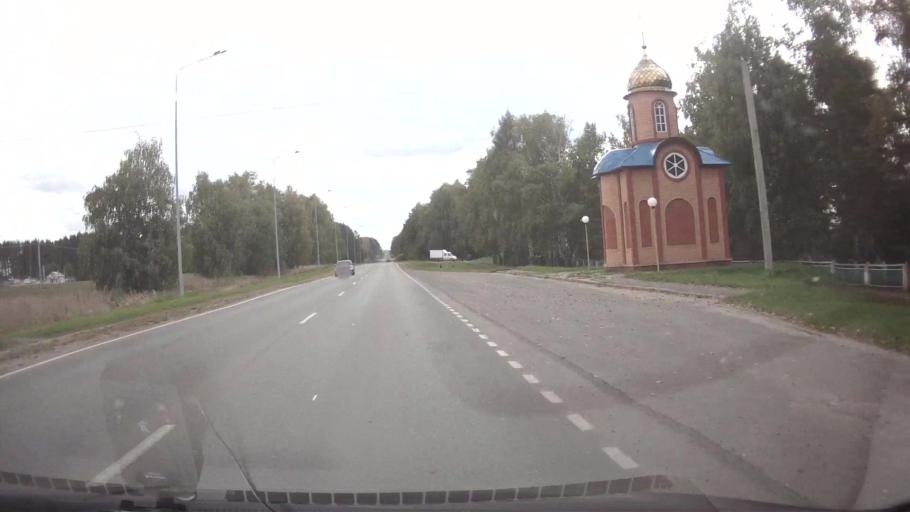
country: RU
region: Mariy-El
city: Kuzhener
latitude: 56.9932
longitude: 48.7428
